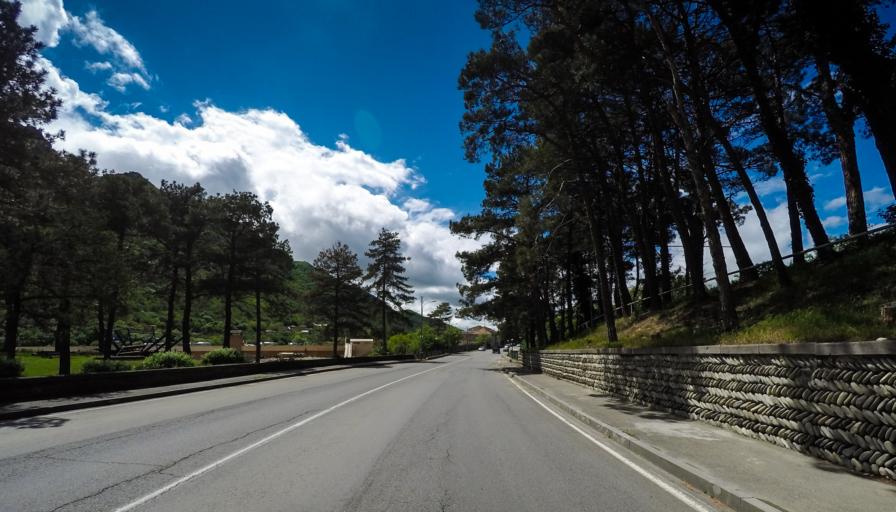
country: GE
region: Mtskheta-Mtianeti
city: Mtskheta
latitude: 41.8392
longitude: 44.7105
